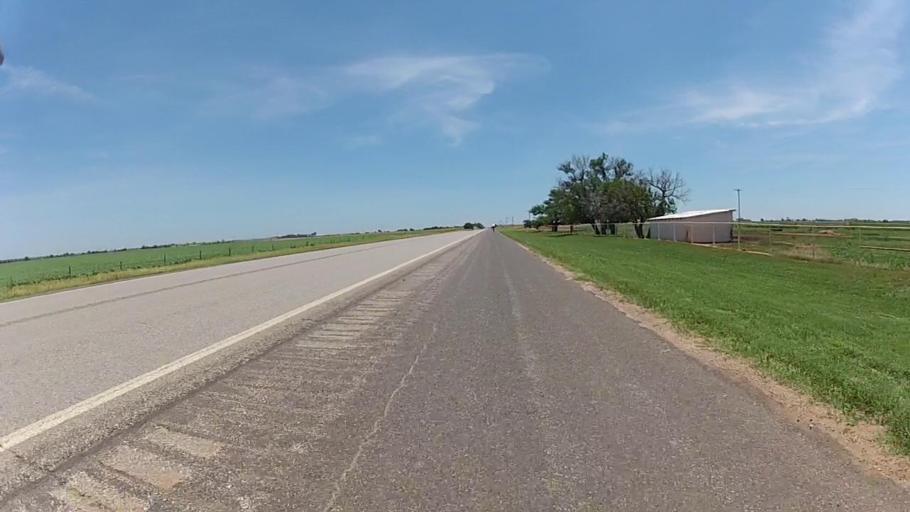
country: US
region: Kansas
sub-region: Barber County
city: Medicine Lodge
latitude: 37.2536
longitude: -98.3963
